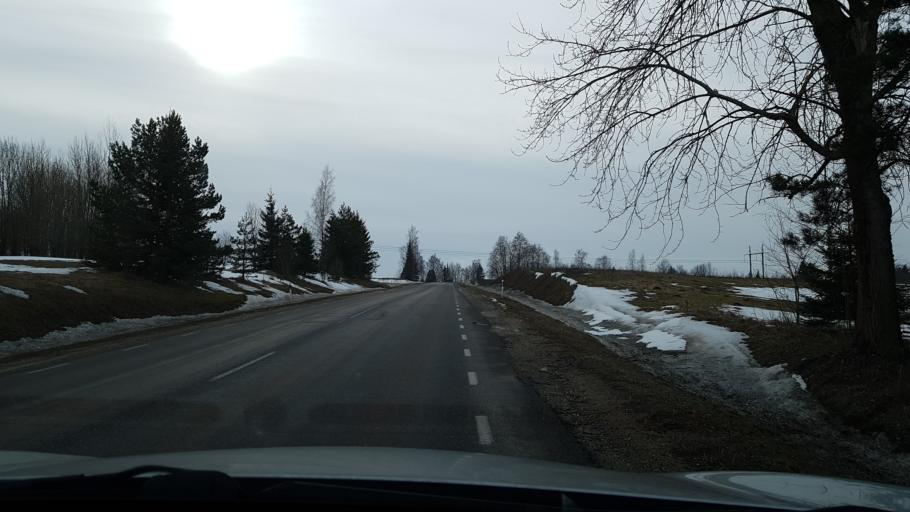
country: EE
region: Tartu
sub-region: Noo vald
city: Noo
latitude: 58.2219
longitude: 26.6302
